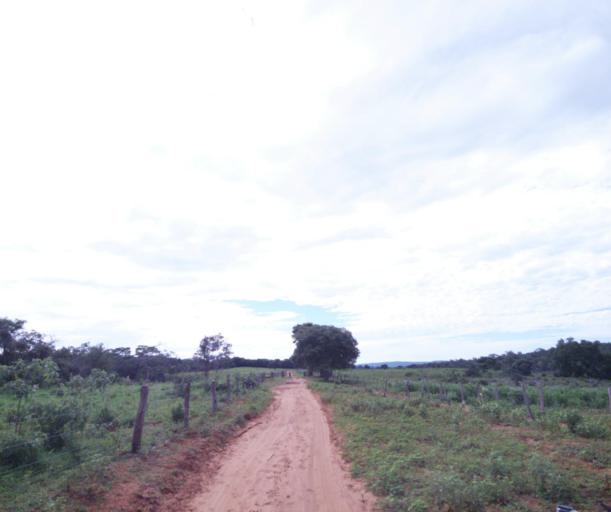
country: BR
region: Bahia
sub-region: Carinhanha
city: Carinhanha
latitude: -14.2136
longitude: -44.4485
